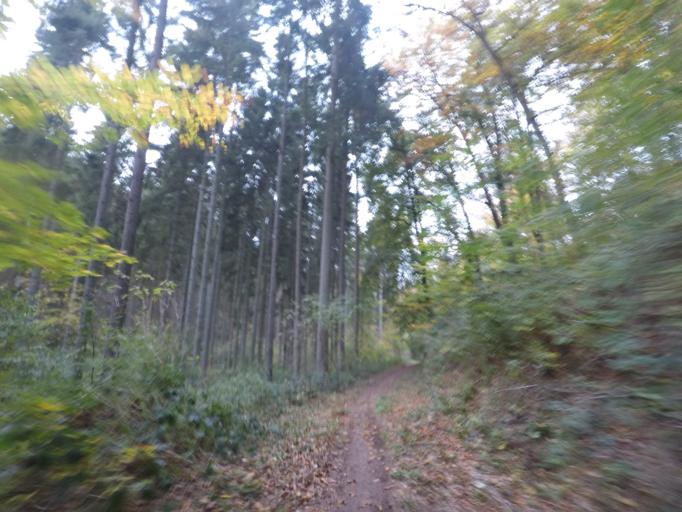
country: LU
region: Luxembourg
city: Itzig
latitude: 49.6051
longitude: 6.1810
